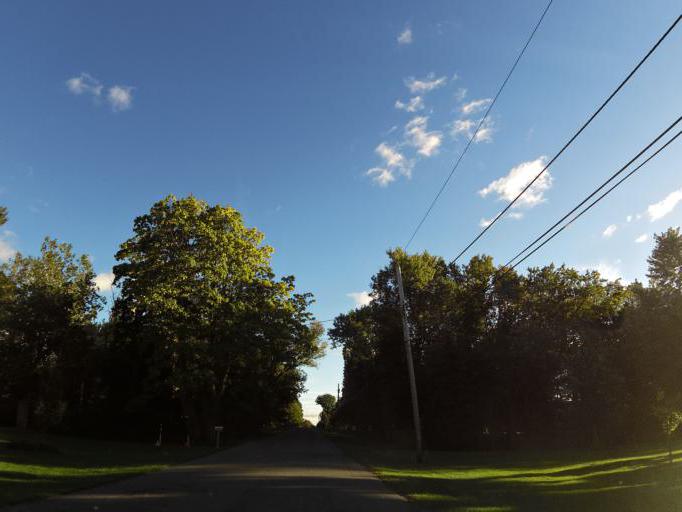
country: US
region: New York
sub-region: Erie County
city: Elma Center
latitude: 42.8171
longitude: -78.6214
